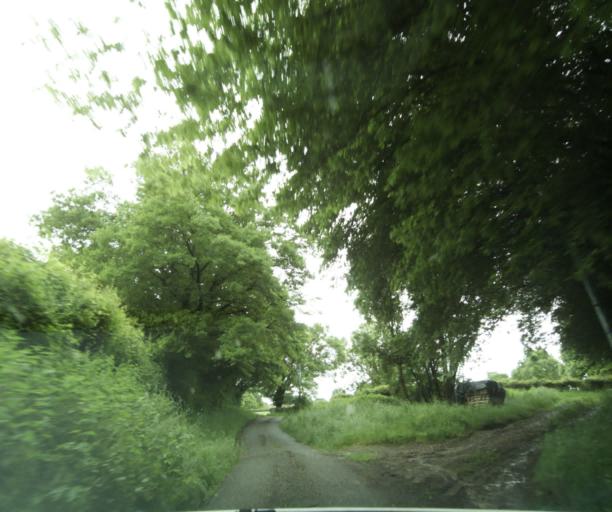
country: FR
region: Bourgogne
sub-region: Departement de Saone-et-Loire
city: Charolles
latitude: 46.4699
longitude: 4.3304
